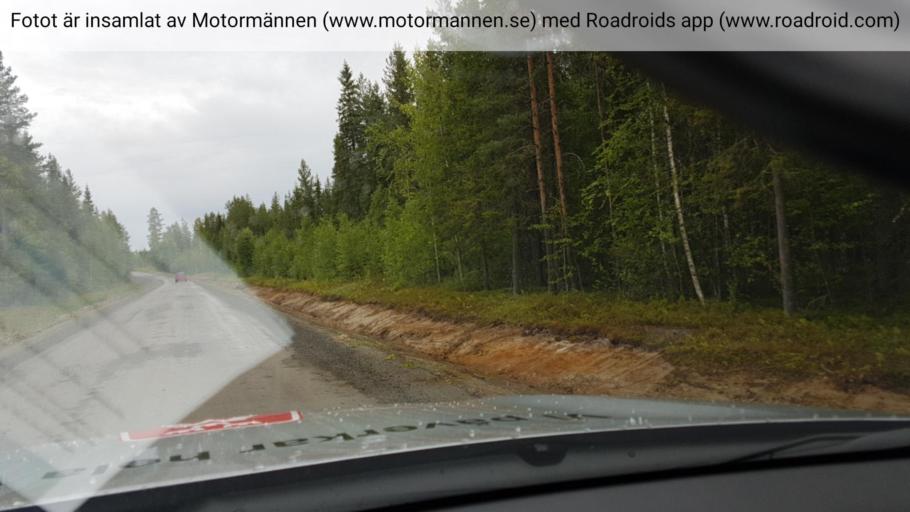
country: SE
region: Norrbotten
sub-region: Alvsbyns Kommun
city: AElvsbyn
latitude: 65.9504
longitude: 21.2320
